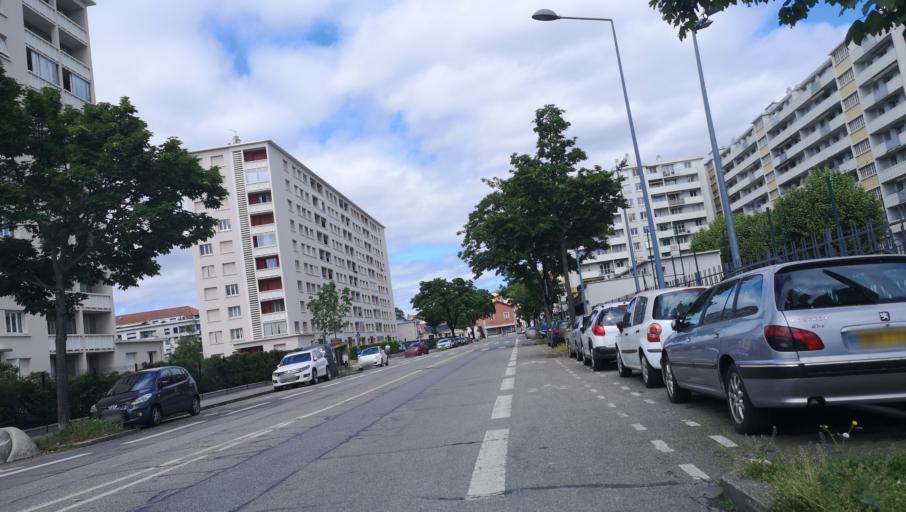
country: FR
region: Rhone-Alpes
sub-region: Departement du Rhone
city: Villeurbanne
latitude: 45.7697
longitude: 4.8849
